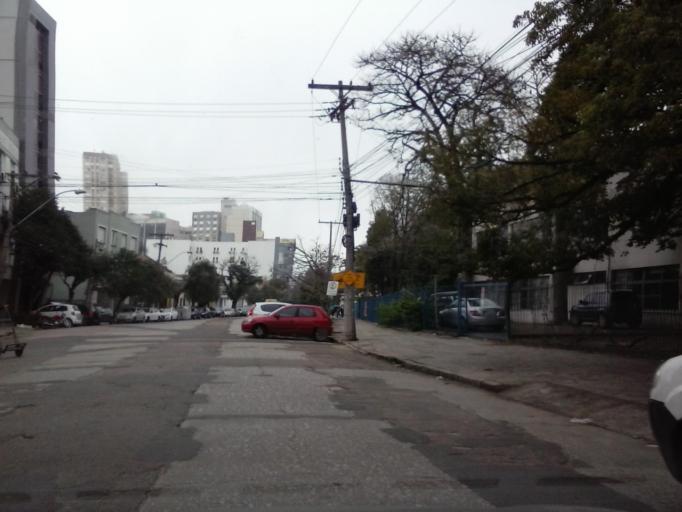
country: BR
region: Rio Grande do Sul
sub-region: Porto Alegre
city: Porto Alegre
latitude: -30.0368
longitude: -51.2322
